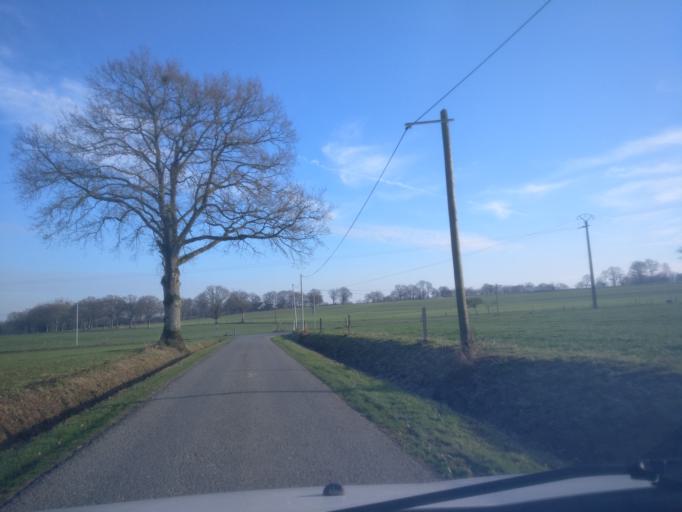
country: FR
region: Brittany
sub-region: Departement d'Ille-et-Vilaine
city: Livre-sur-Changeon
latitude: 48.2138
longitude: -1.3046
